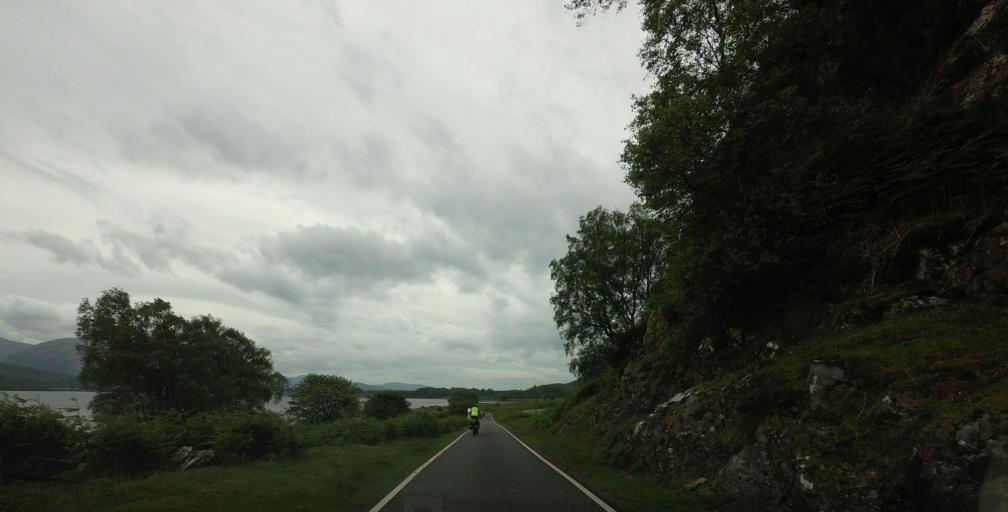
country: GB
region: Scotland
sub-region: Highland
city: Fort William
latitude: 56.7428
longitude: -5.2459
